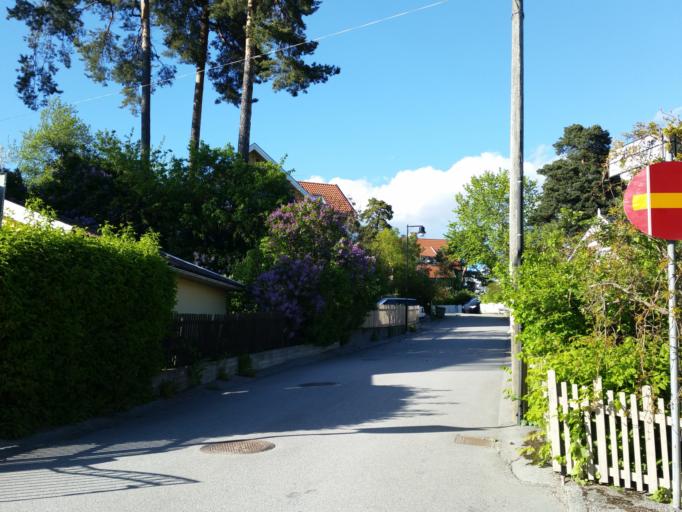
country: SE
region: Stockholm
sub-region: Sundbybergs Kommun
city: Sundbyberg
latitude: 59.3711
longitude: 17.9606
